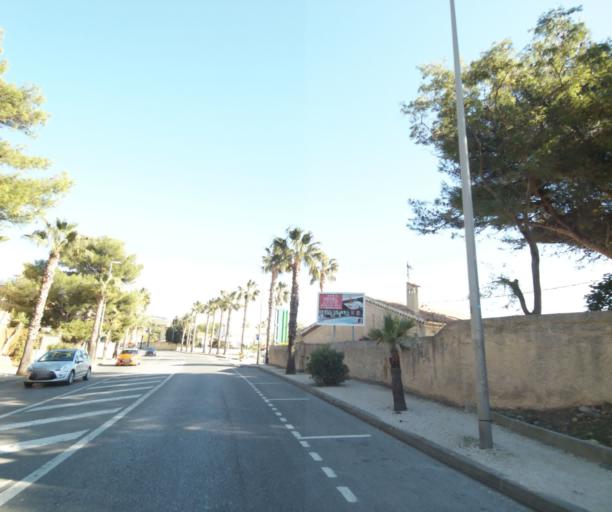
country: FR
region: Provence-Alpes-Cote d'Azur
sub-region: Departement des Bouches-du-Rhone
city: Ceyreste
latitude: 43.1889
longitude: 5.6332
